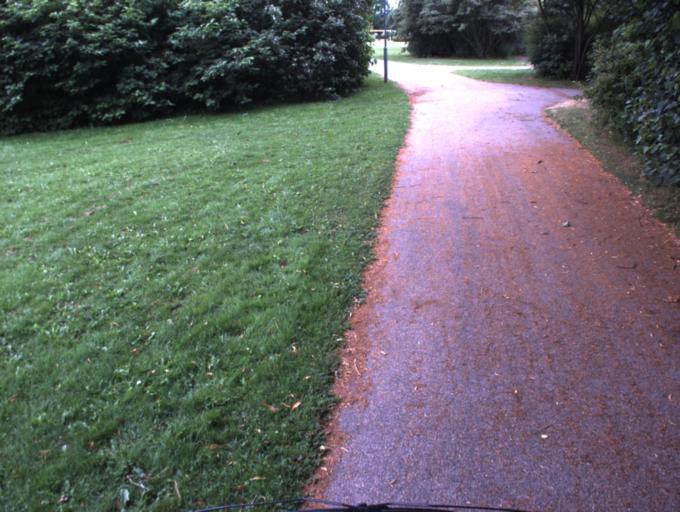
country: SE
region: Skane
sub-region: Helsingborg
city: Helsingborg
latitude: 56.0713
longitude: 12.7070
